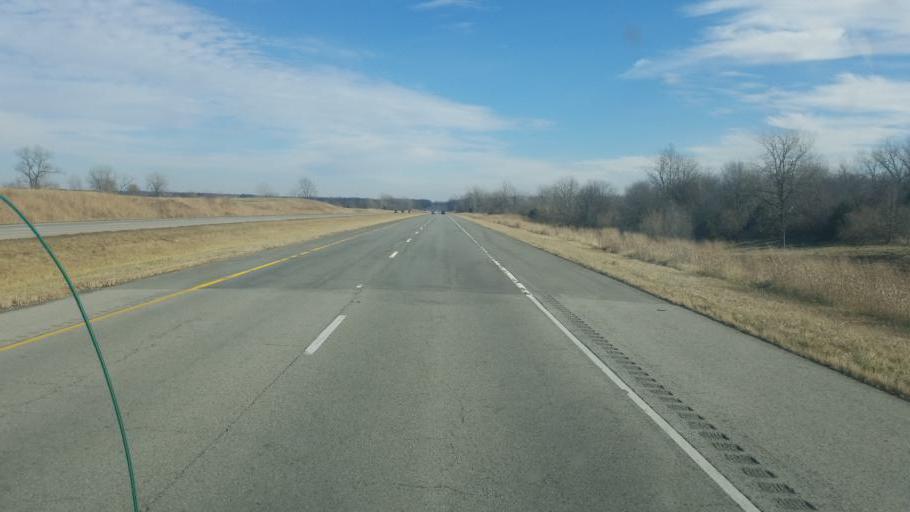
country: US
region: Illinois
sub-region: Saline County
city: Carrier Mills
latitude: 37.7303
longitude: -88.7735
